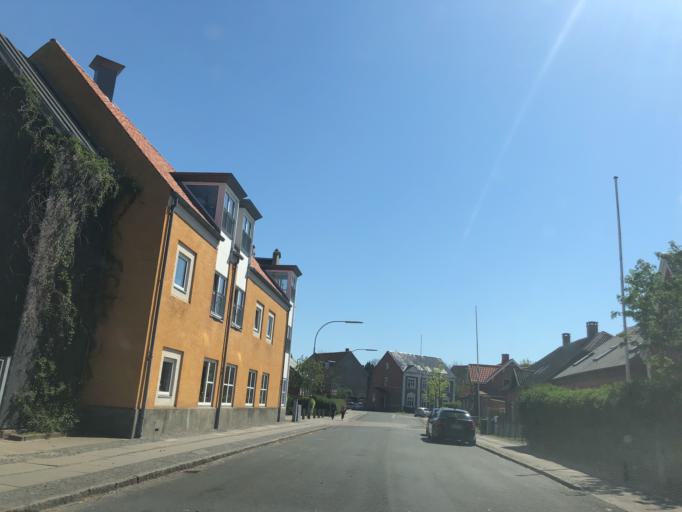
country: DK
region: Zealand
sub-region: Slagelse Kommune
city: Korsor
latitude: 55.3282
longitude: 11.1420
